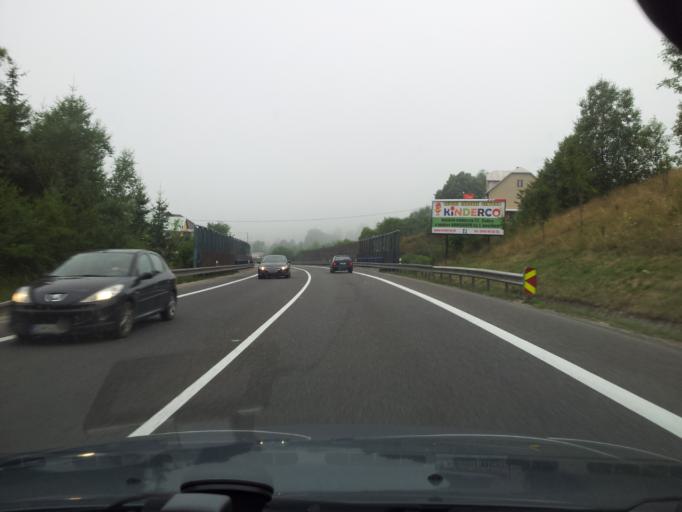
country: SK
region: Zilinsky
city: Cadca
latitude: 49.4252
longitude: 18.8349
